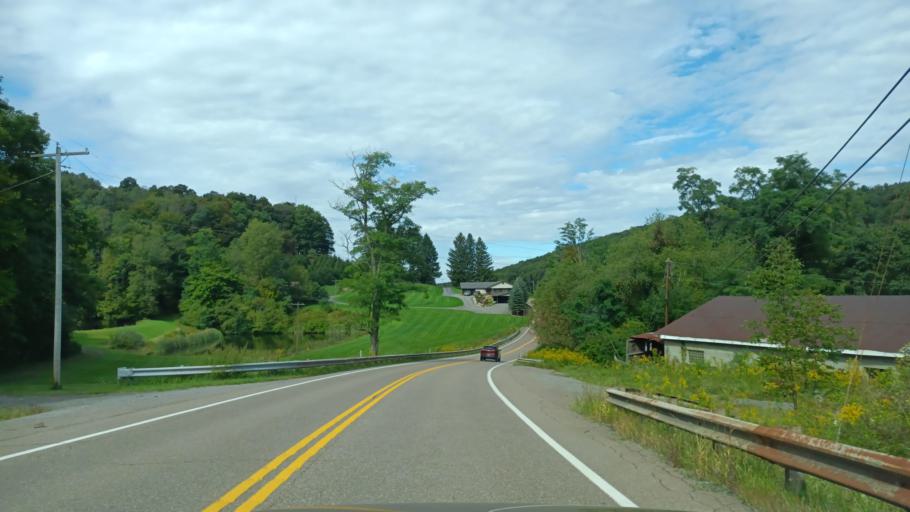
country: US
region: Maryland
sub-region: Garrett County
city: Mountain Lake Park
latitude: 39.2972
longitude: -79.4342
